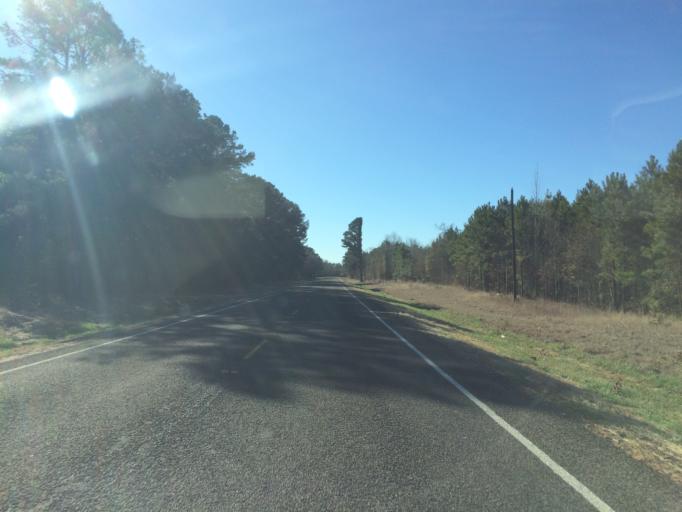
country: US
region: Texas
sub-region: Wood County
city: Hawkins
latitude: 32.6136
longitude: -95.2741
